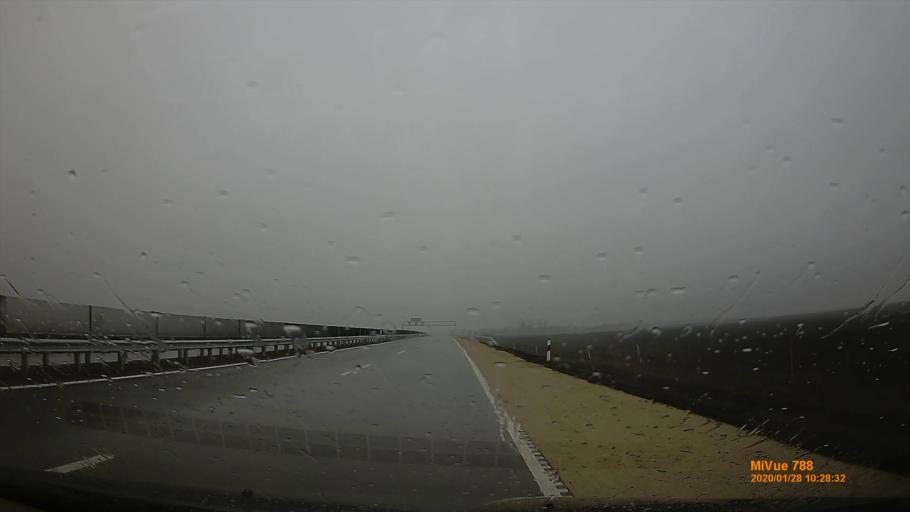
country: HU
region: Pest
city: Pilis
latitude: 47.3171
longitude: 19.5460
